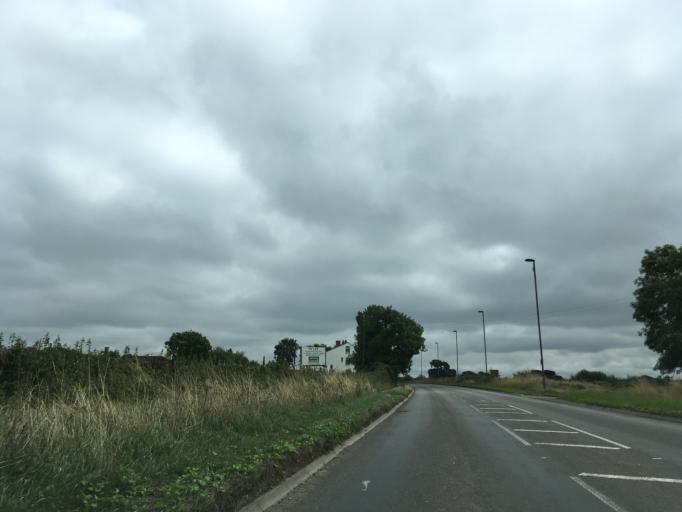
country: GB
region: England
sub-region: South Gloucestershire
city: Yate
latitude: 51.5498
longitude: -2.4573
